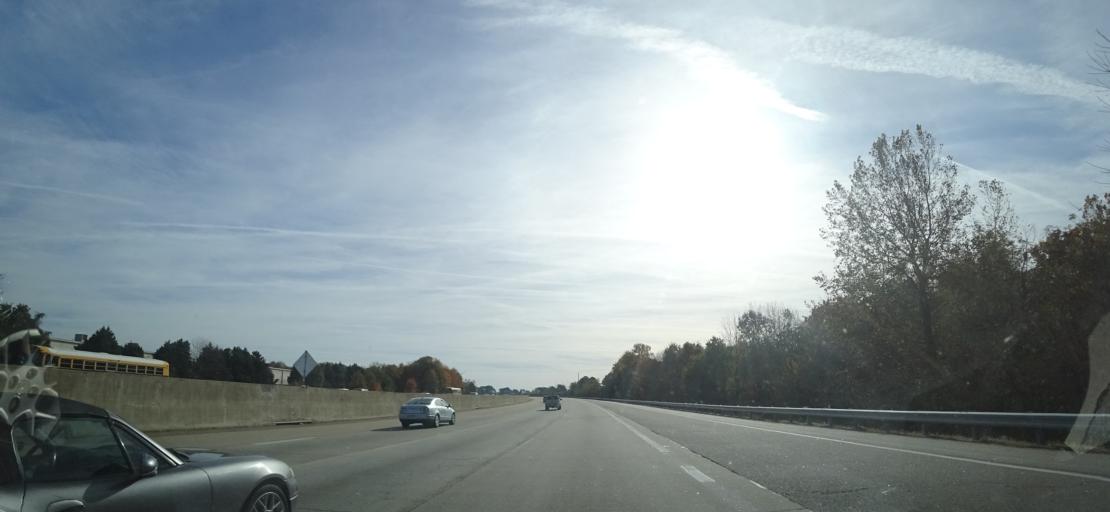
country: US
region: Virginia
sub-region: York County
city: Yorktown
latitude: 37.1210
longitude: -76.5145
